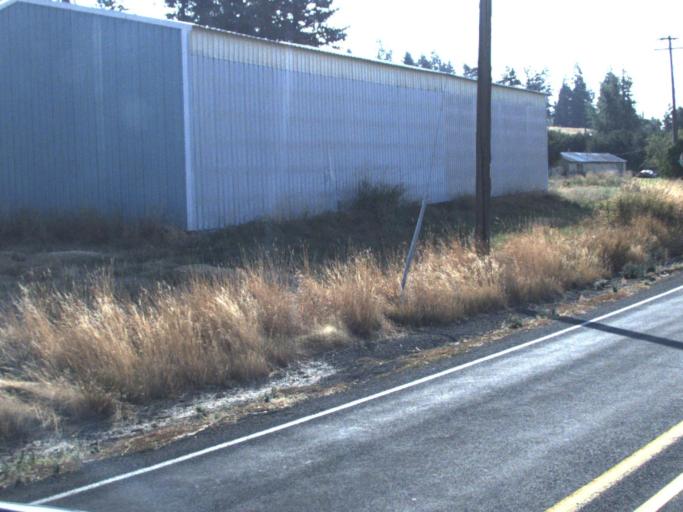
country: US
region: Idaho
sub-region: Benewah County
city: Plummer
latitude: 47.2842
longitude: -117.1616
